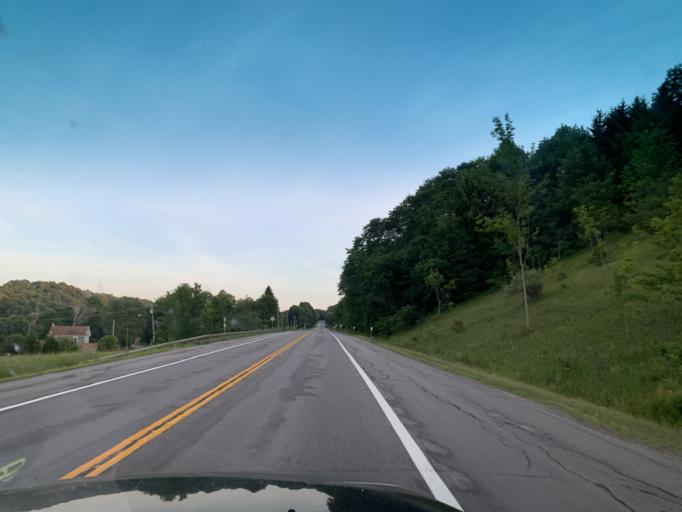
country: US
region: New York
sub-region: Oneida County
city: Chadwicks
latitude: 42.9844
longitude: -75.2537
